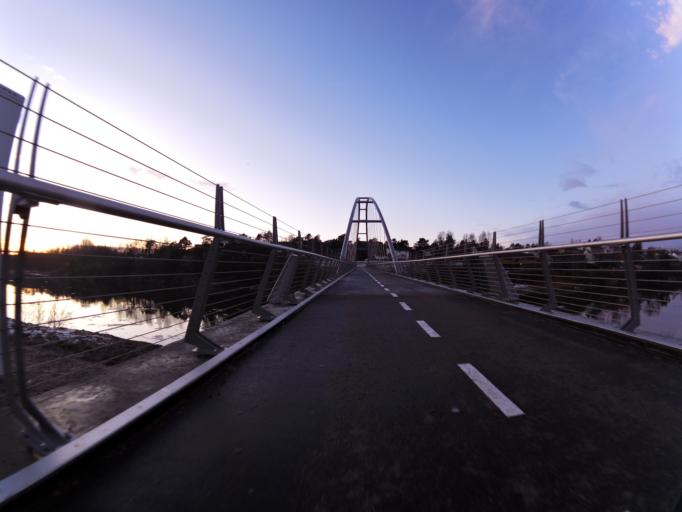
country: NO
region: Ostfold
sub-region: Sarpsborg
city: Sarpsborg
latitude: 59.2906
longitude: 11.1383
